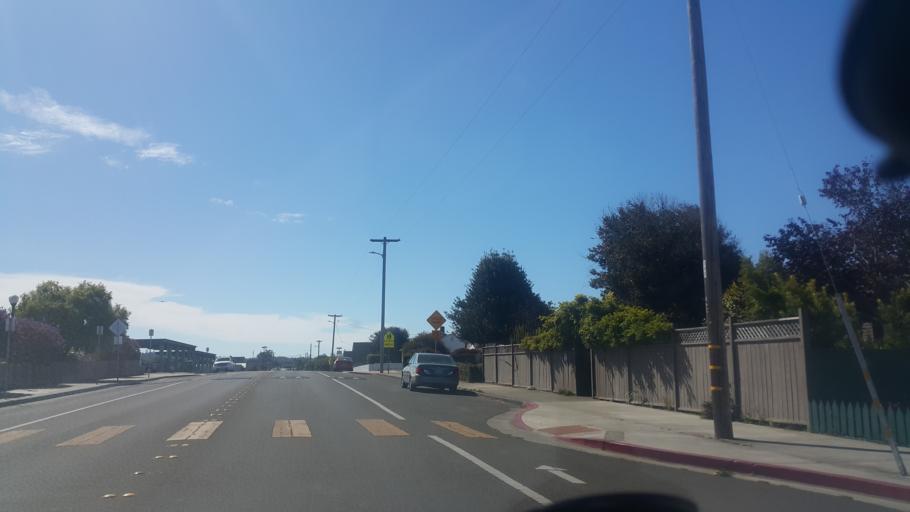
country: US
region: California
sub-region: Mendocino County
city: Fort Bragg
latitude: 39.4480
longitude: -123.7982
